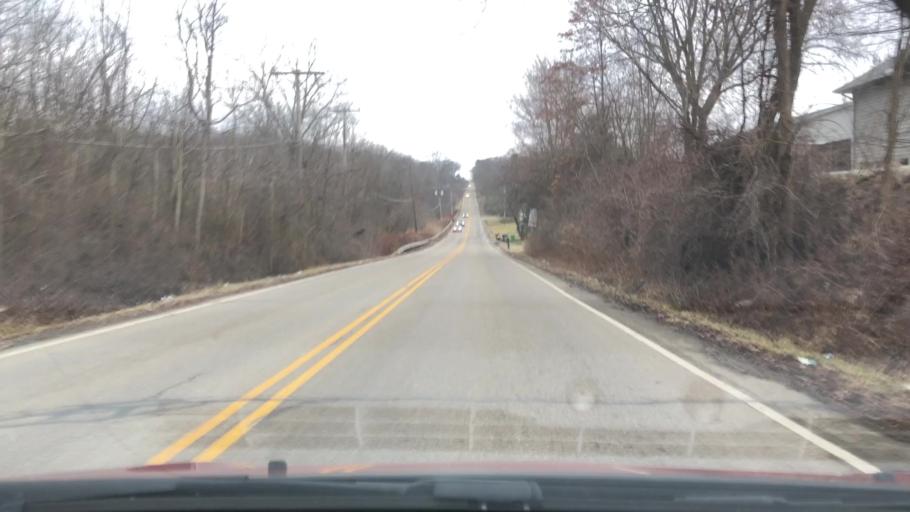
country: US
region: Ohio
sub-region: Summit County
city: Norton
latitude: 40.9886
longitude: -81.6393
